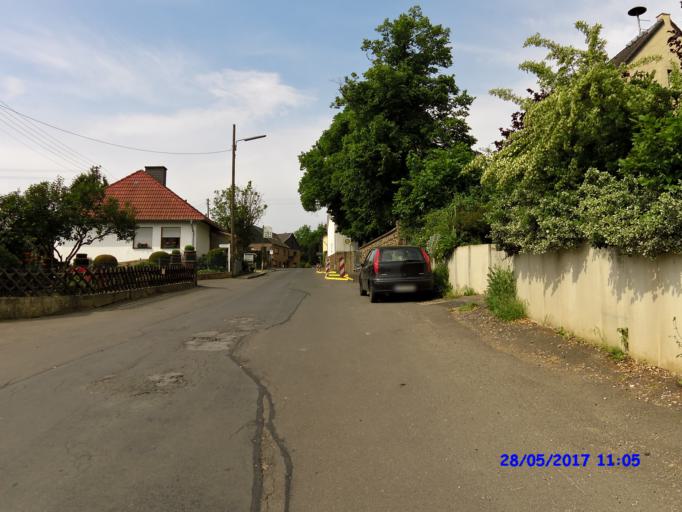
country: DE
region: Rheinland-Pfalz
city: Berg
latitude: 50.5510
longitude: 6.9330
